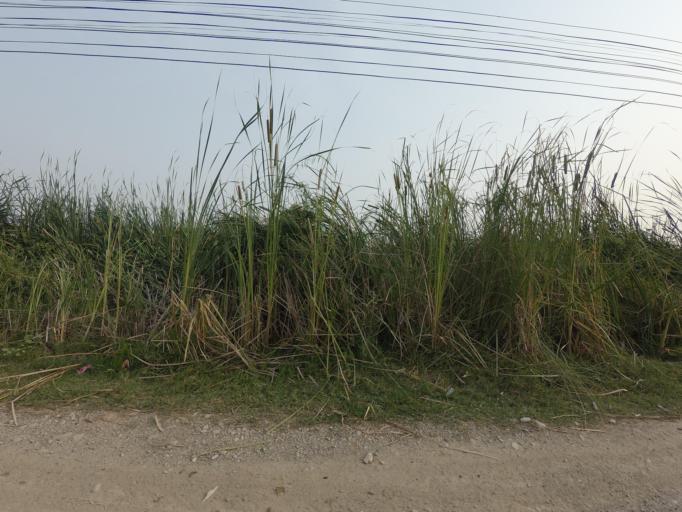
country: NP
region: Western Region
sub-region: Lumbini Zone
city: Bhairahawa
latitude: 27.5079
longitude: 83.4592
